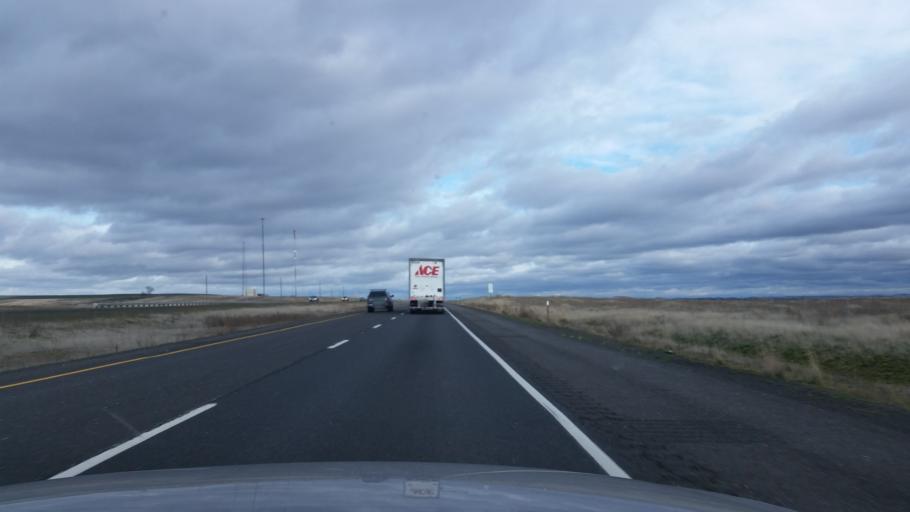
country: US
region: Washington
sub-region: Spokane County
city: Medical Lake
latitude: 47.3124
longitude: -117.9632
